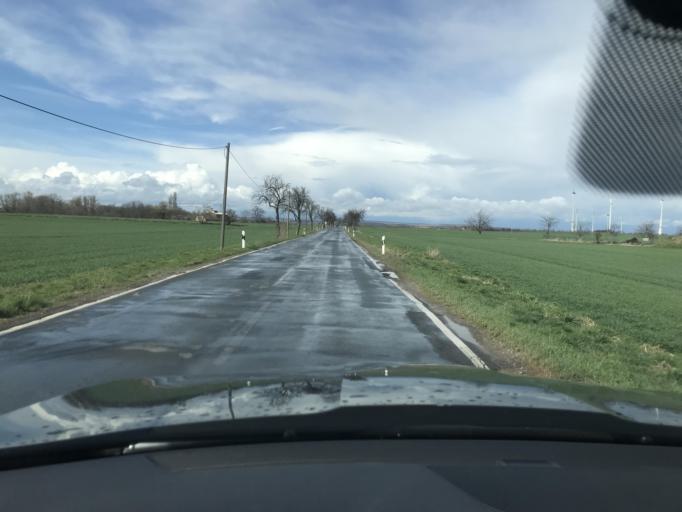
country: DE
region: Saxony-Anhalt
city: Frose
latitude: 51.7431
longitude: 11.3654
